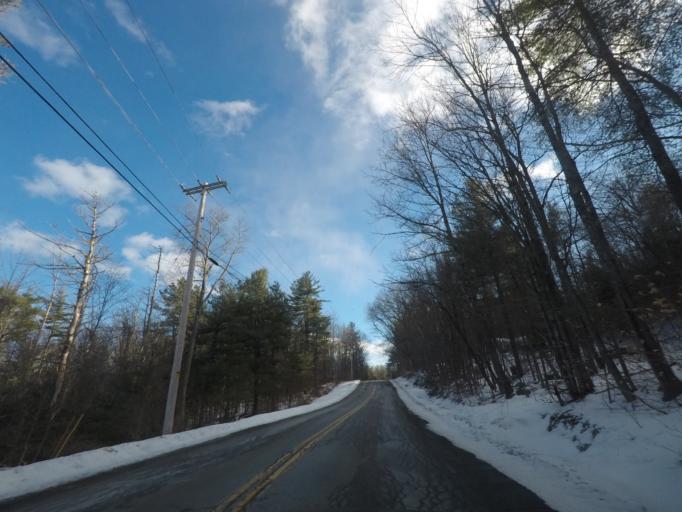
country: US
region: New York
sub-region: Rensselaer County
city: Hoosick Falls
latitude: 42.8149
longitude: -73.3910
